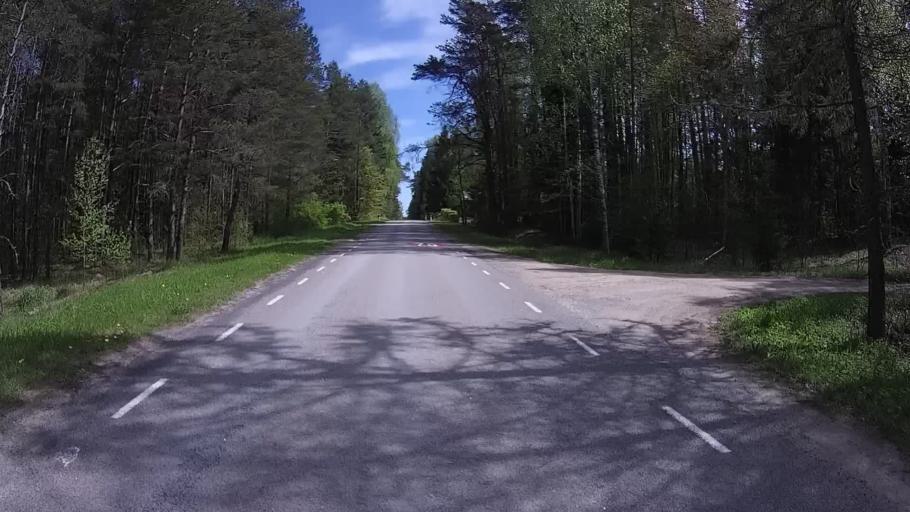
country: LV
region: Apes Novads
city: Ape
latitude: 57.6103
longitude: 26.4439
